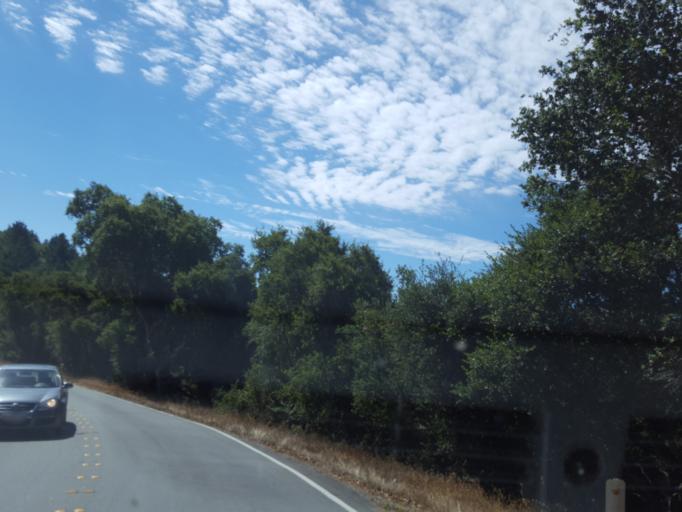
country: US
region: California
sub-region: San Mateo County
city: Portola Valley
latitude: 37.2971
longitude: -122.2803
